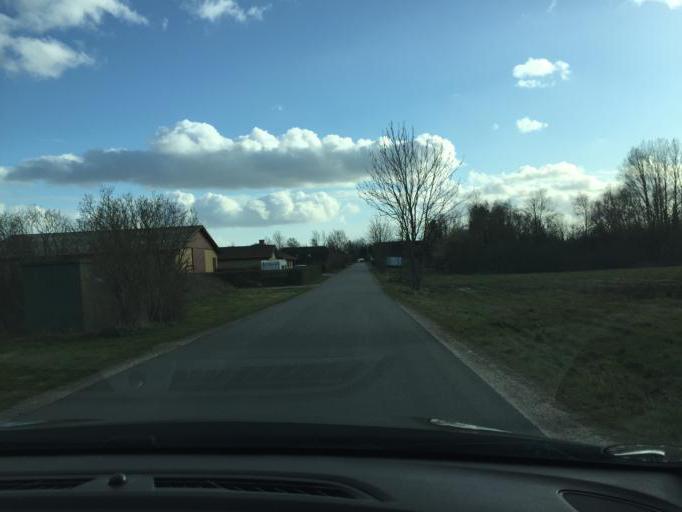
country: DK
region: South Denmark
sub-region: Nyborg Kommune
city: Ullerslev
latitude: 55.3614
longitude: 10.6307
